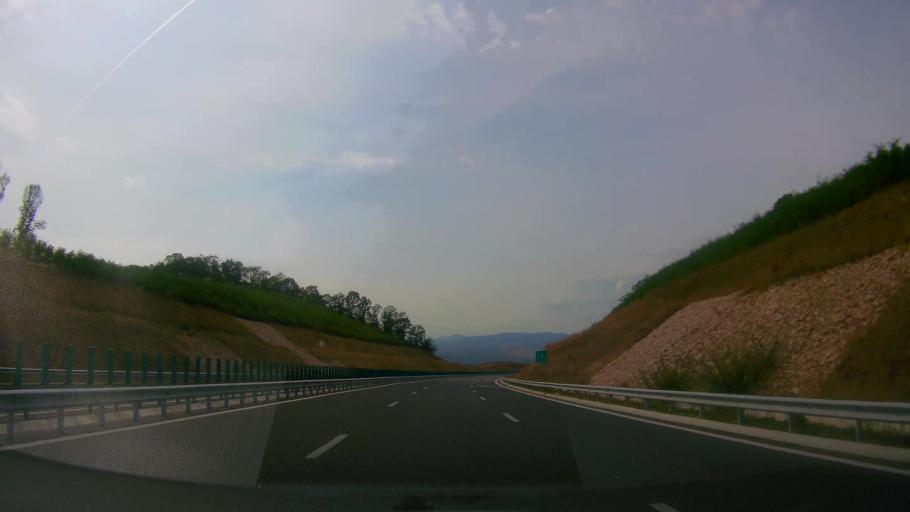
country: RO
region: Cluj
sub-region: Comuna Floresti
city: Luna de Sus
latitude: 46.7827
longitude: 23.4158
